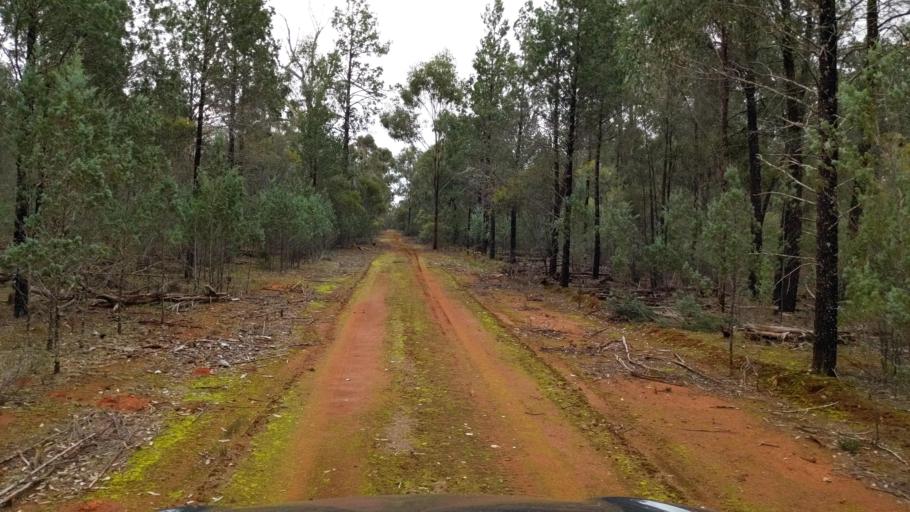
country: AU
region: New South Wales
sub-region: Coolamon
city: Coolamon
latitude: -34.8364
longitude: 146.9345
